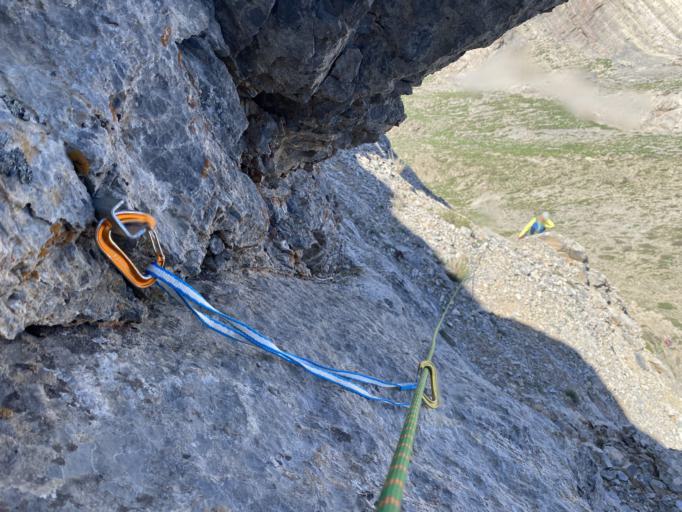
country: KZ
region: Ongtustik Qazaqstan
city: Kentau
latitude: 43.9602
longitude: 68.2466
